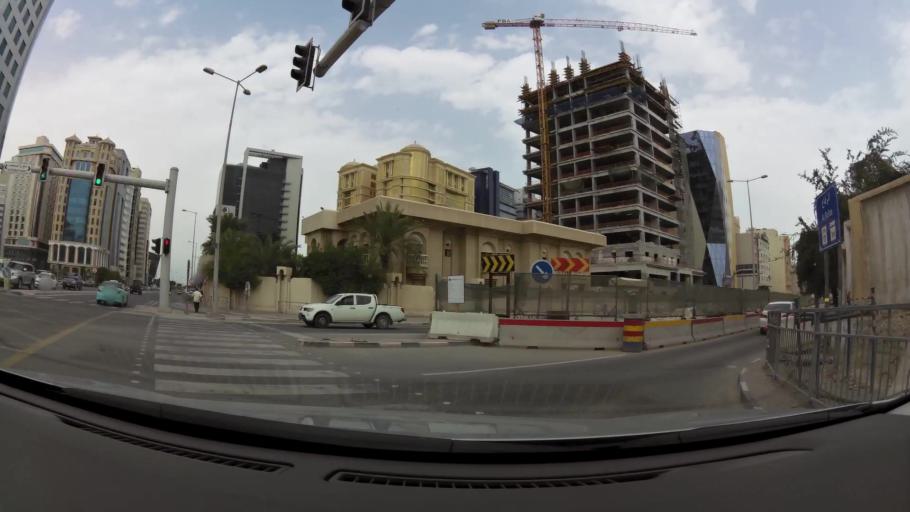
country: QA
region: Baladiyat ad Dawhah
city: Doha
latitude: 25.2867
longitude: 51.5442
